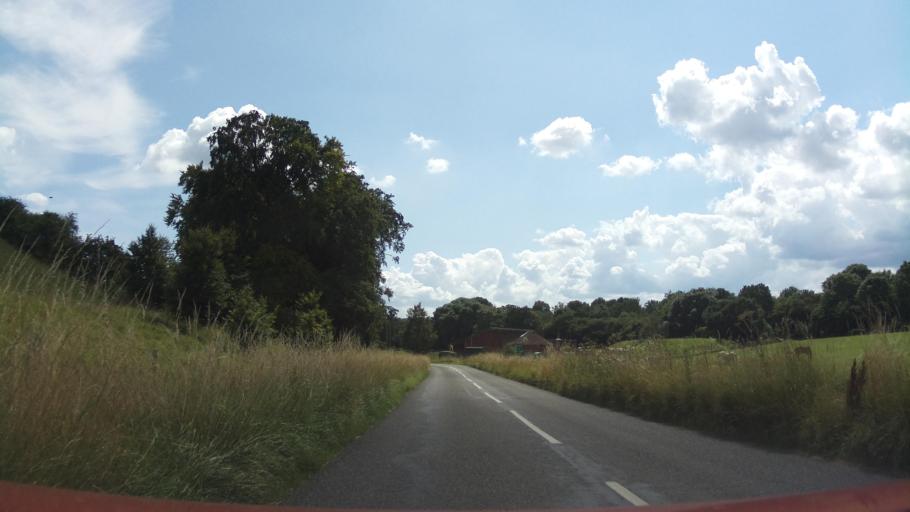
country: GB
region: England
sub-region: Wiltshire
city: Aldbourne
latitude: 51.5305
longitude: -1.5863
